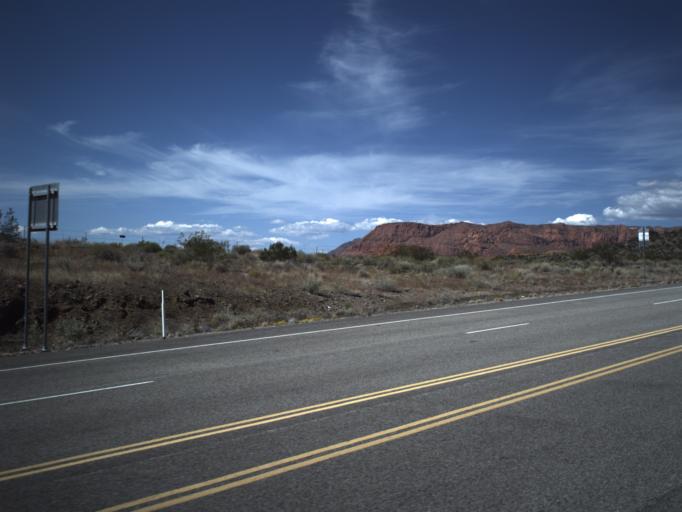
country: US
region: Utah
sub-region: Washington County
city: Saint George
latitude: 37.1402
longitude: -113.6042
